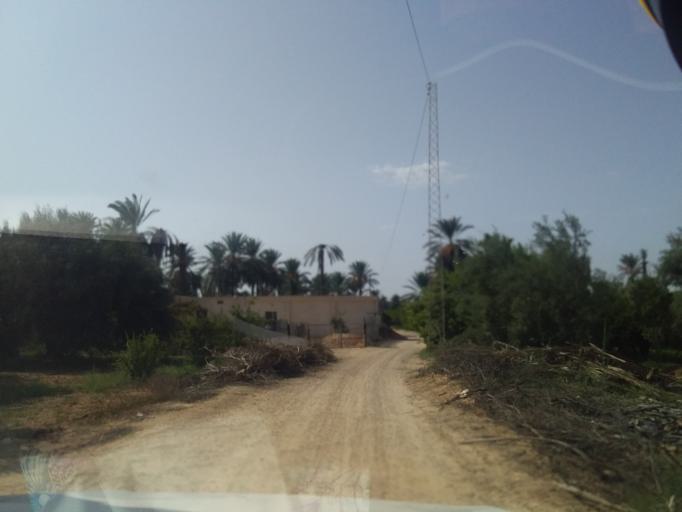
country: TN
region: Qabis
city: Gabes
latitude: 33.6278
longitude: 10.2907
